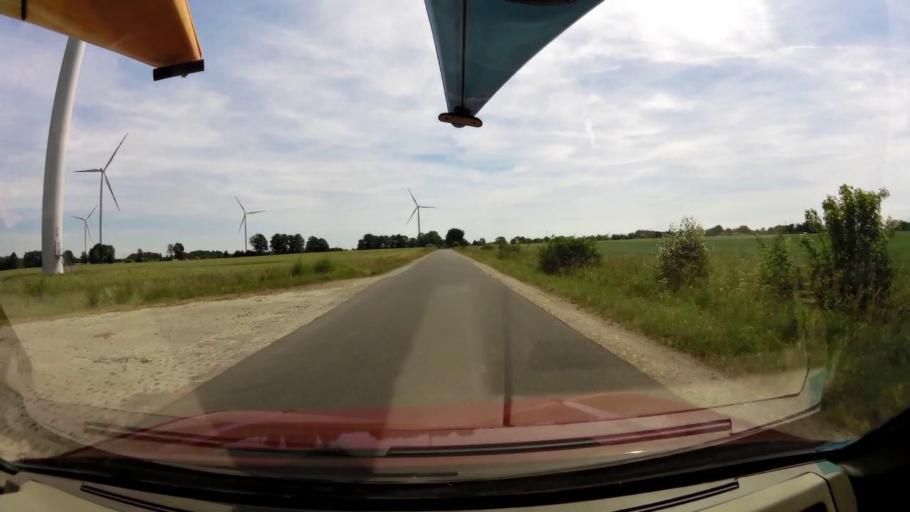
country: PL
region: West Pomeranian Voivodeship
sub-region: Powiat slawienski
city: Darlowo
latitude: 54.3123
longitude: 16.4724
